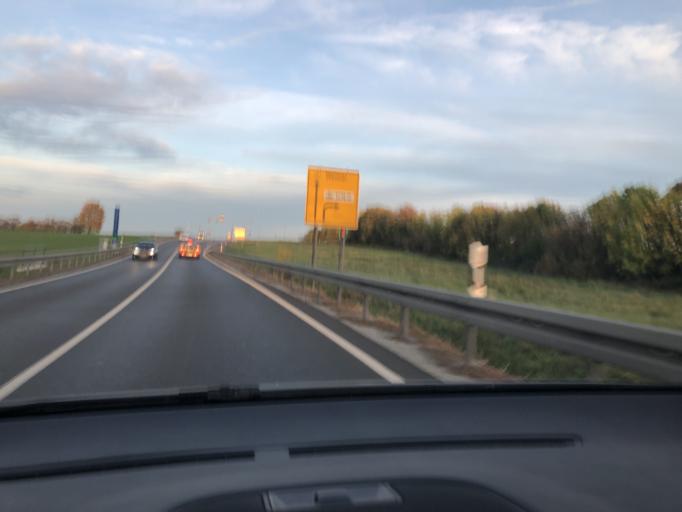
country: DE
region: Thuringia
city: Hopfgarten
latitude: 50.9673
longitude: 11.2547
